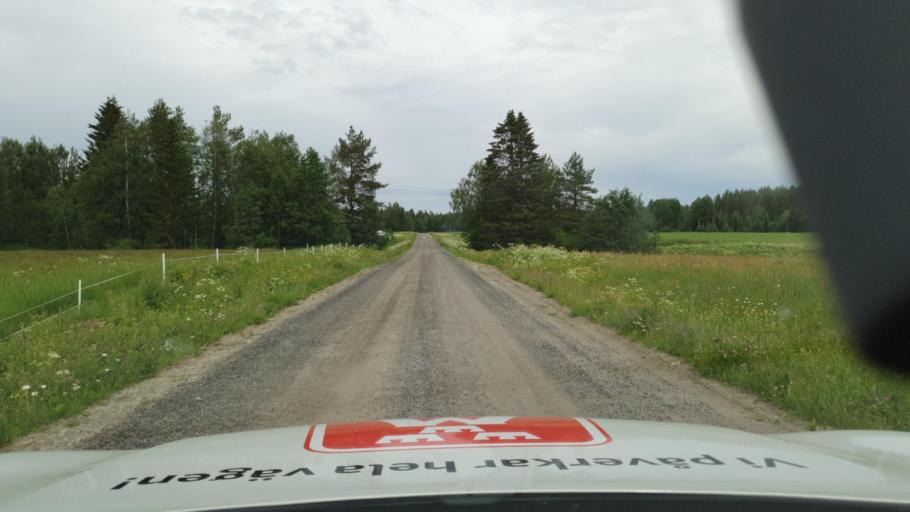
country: SE
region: Vaesterbotten
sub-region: Robertsfors Kommun
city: Robertsfors
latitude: 64.1868
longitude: 20.7284
